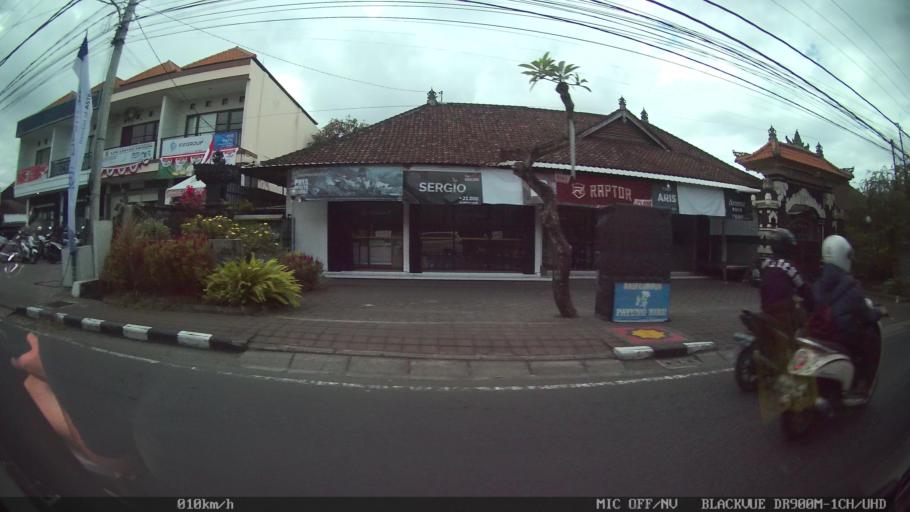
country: ID
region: Bali
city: Banjar Pekenjelodan
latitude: -8.5851
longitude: 115.1801
